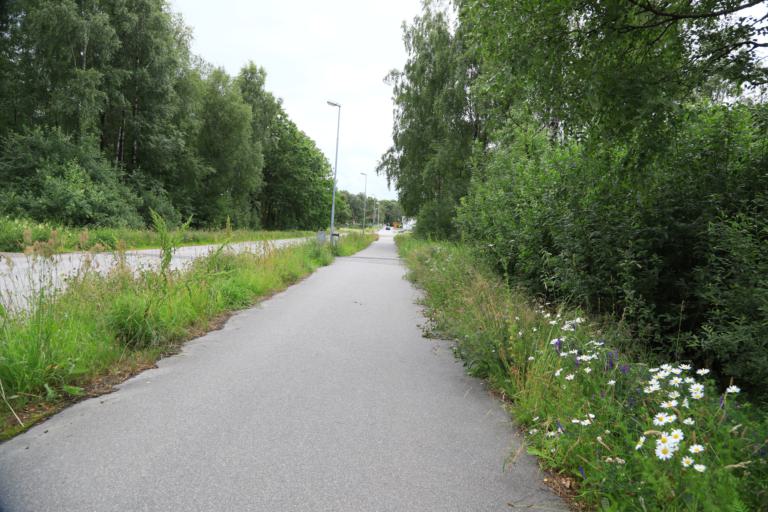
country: SE
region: Halland
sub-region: Varbergs Kommun
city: Traslovslage
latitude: 57.1019
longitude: 12.2974
